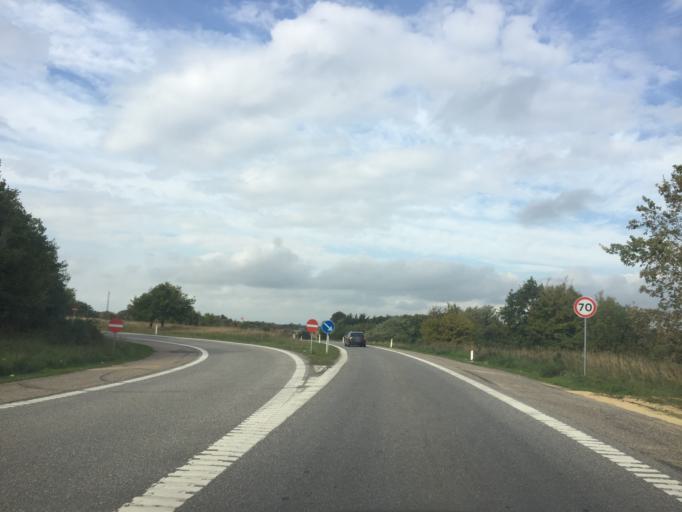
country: DK
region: Zealand
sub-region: Vordingborg Kommune
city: Praesto
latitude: 55.1647
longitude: 11.9611
